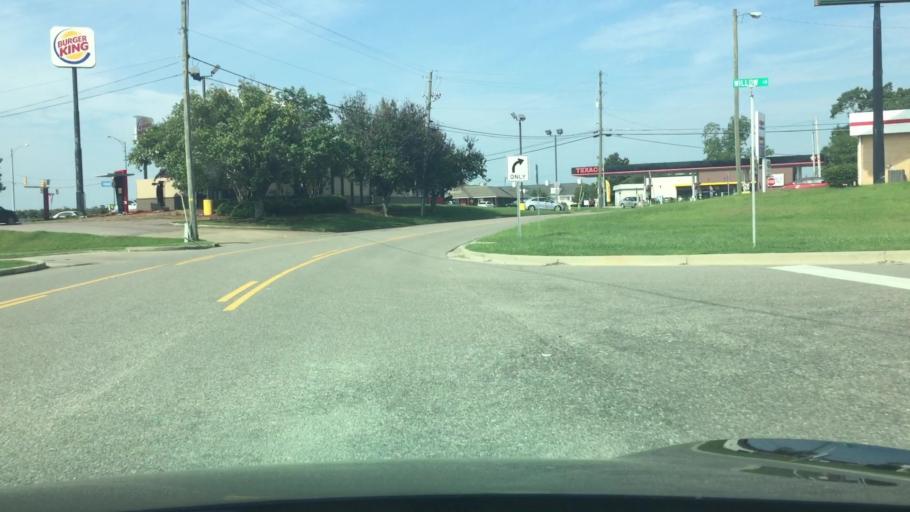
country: US
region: Alabama
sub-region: Butler County
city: Greenville
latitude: 31.8529
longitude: -86.6400
